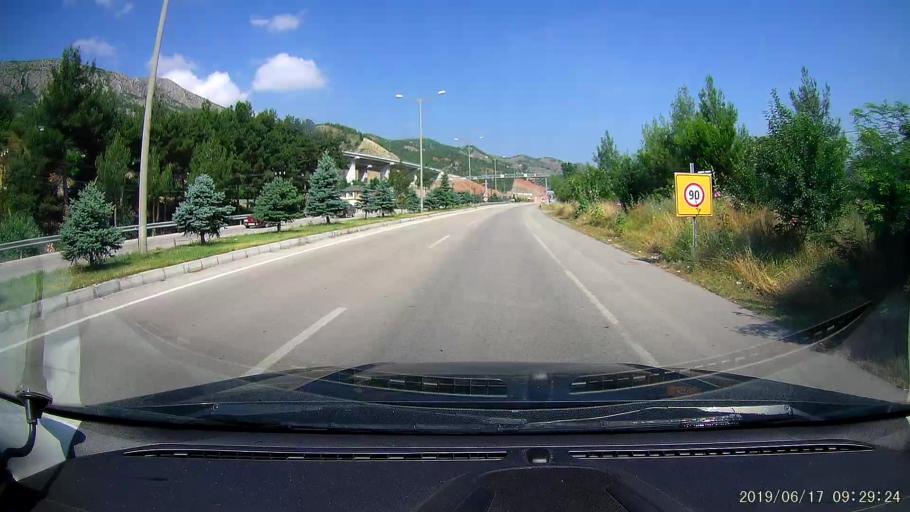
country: TR
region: Amasya
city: Amasya
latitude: 40.6962
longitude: 35.8127
